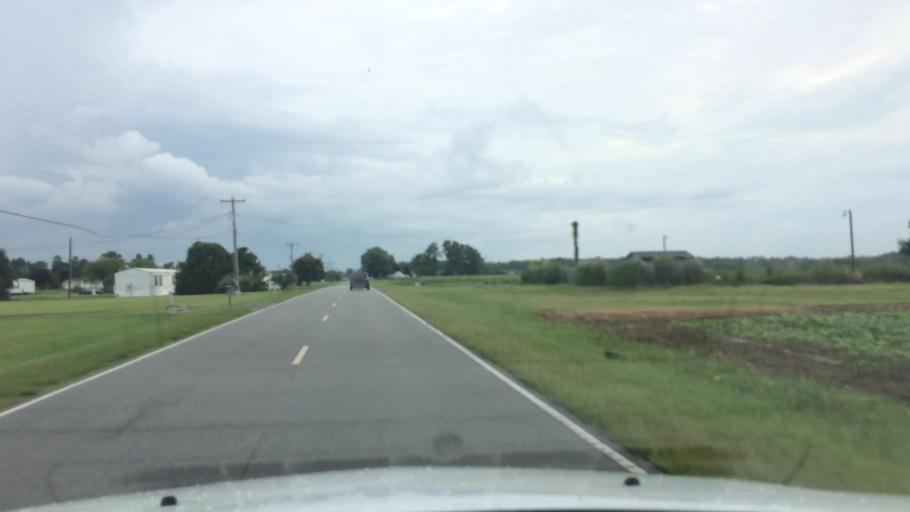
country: US
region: North Carolina
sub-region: Pitt County
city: Farmville
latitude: 35.5585
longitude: -77.5460
